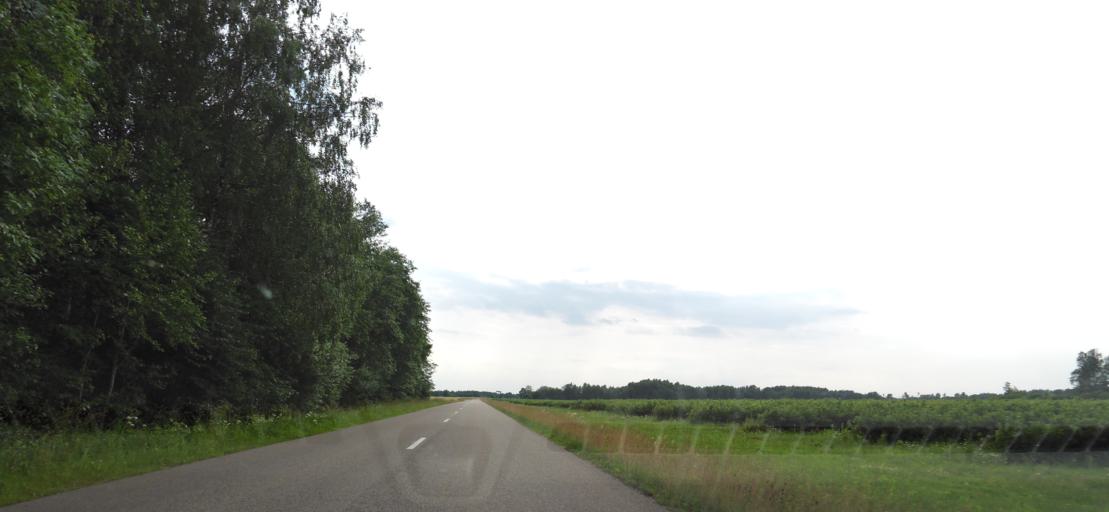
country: LT
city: Obeliai
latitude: 56.1108
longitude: 25.0683
